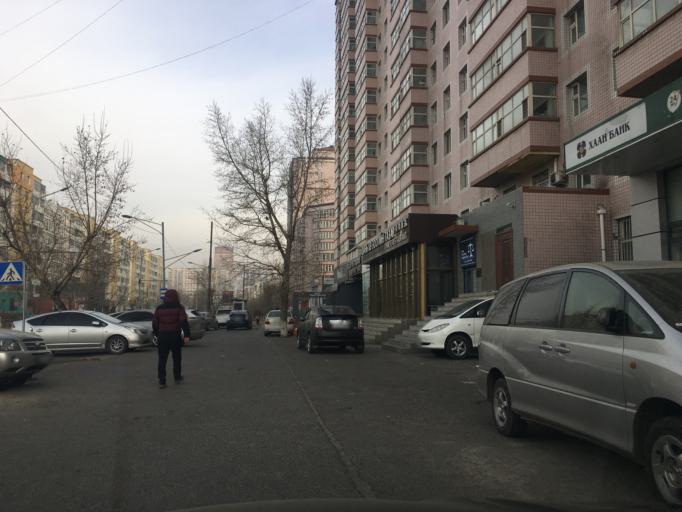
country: MN
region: Ulaanbaatar
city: Ulaanbaatar
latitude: 47.9114
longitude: 106.8841
